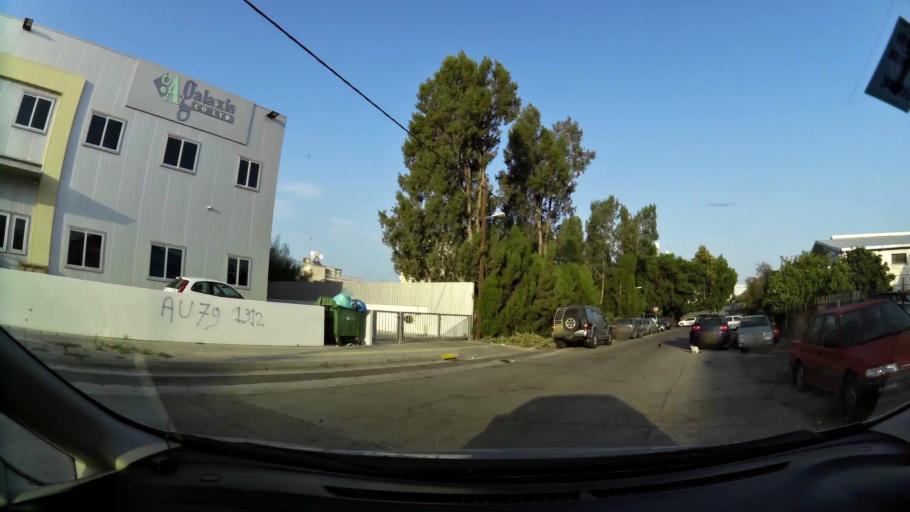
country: CY
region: Lefkosia
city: Nicosia
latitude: 35.1678
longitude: 33.3252
